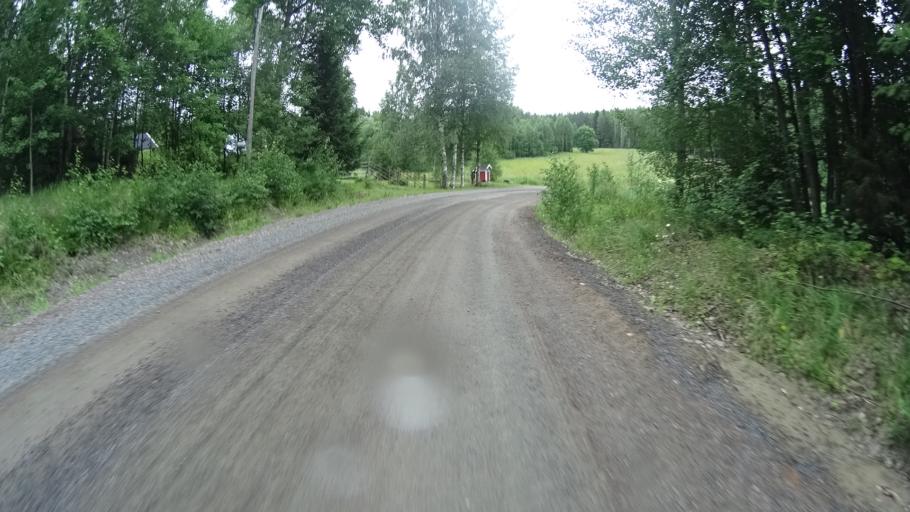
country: FI
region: Uusimaa
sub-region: Helsinki
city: Karkkila
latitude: 60.5984
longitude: 24.1891
